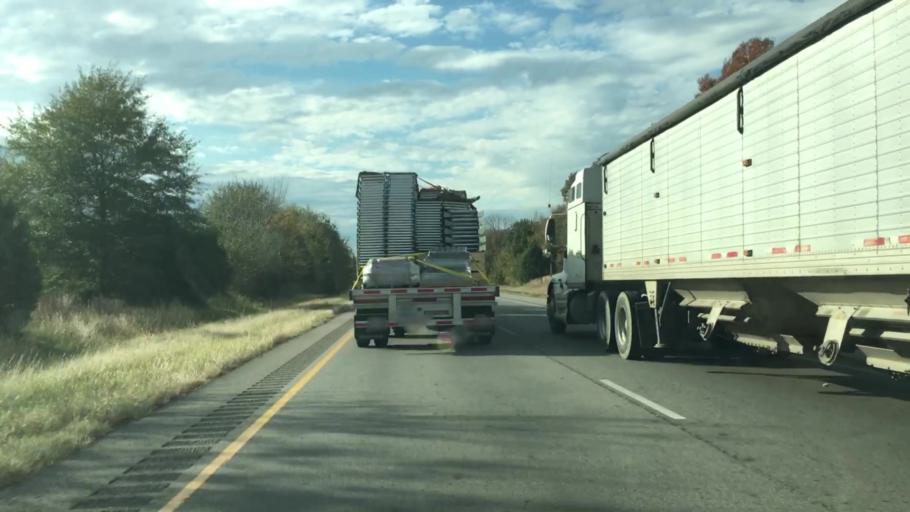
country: US
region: Arkansas
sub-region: Pope County
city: Pottsville
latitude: 35.2468
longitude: -93.0031
